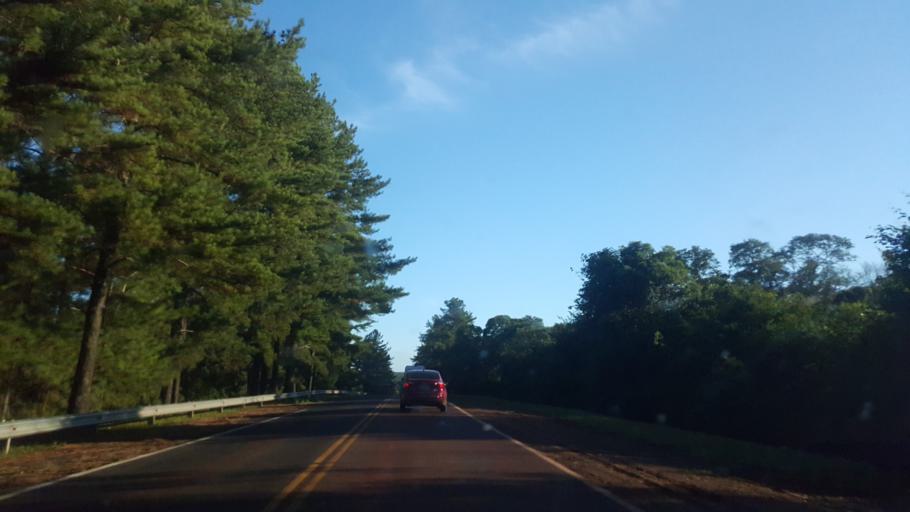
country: AR
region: Misiones
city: El Alcazar
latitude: -26.7502
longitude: -54.8838
